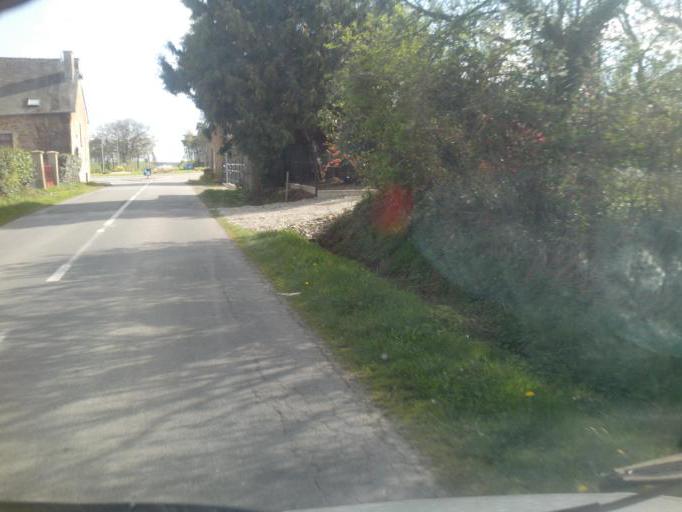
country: FR
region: Brittany
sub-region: Departement d'Ille-et-Vilaine
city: Maure-de-Bretagne
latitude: 47.9099
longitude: -1.9916
